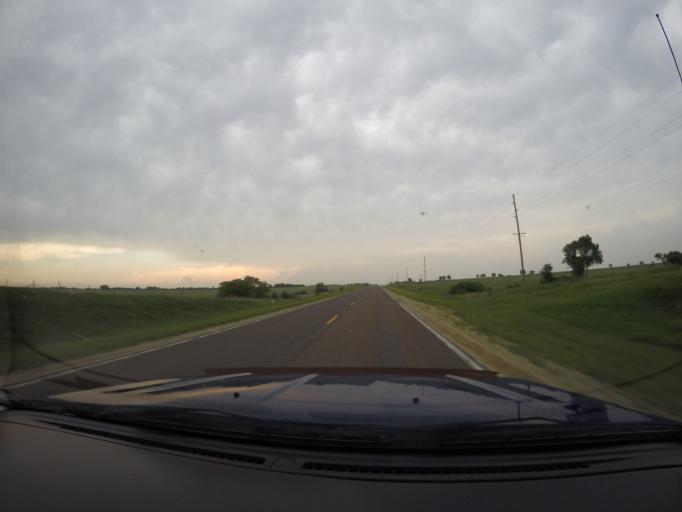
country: US
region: Kansas
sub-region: Clay County
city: Clay Center
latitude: 39.3236
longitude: -96.9235
